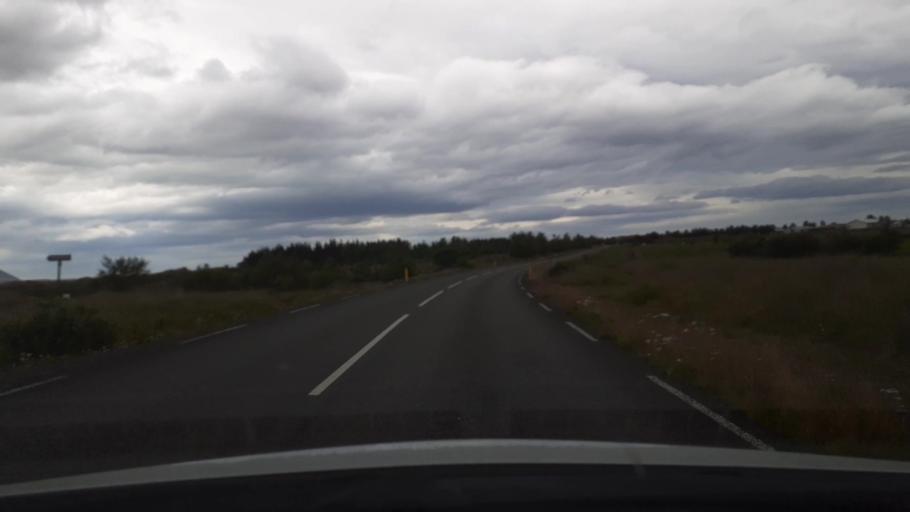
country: IS
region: West
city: Borgarnes
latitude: 64.5595
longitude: -21.7489
